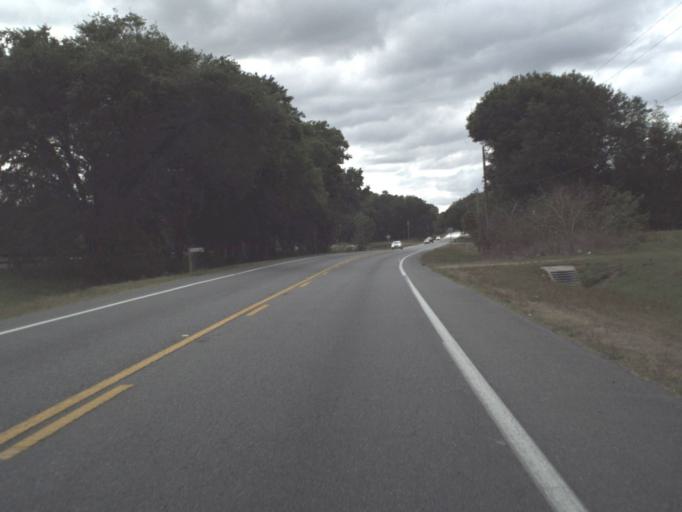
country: US
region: Florida
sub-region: Marion County
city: Ocala
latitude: 29.2593
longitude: -82.1174
